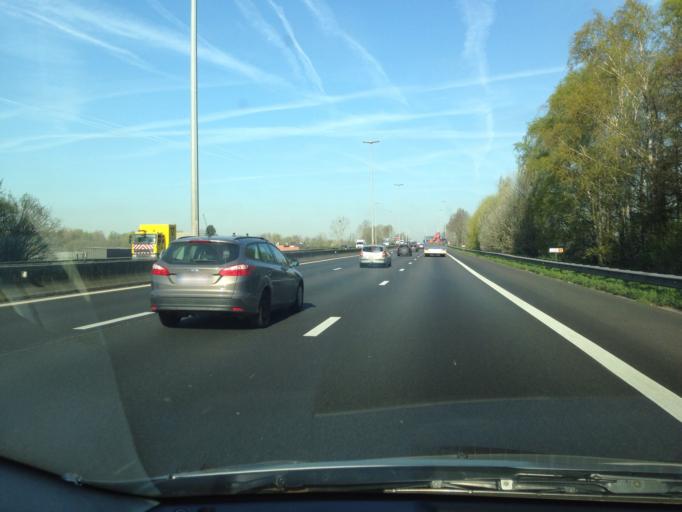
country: BE
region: Flanders
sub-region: Provincie Oost-Vlaanderen
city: Nevele
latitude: 51.0495
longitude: 3.5752
